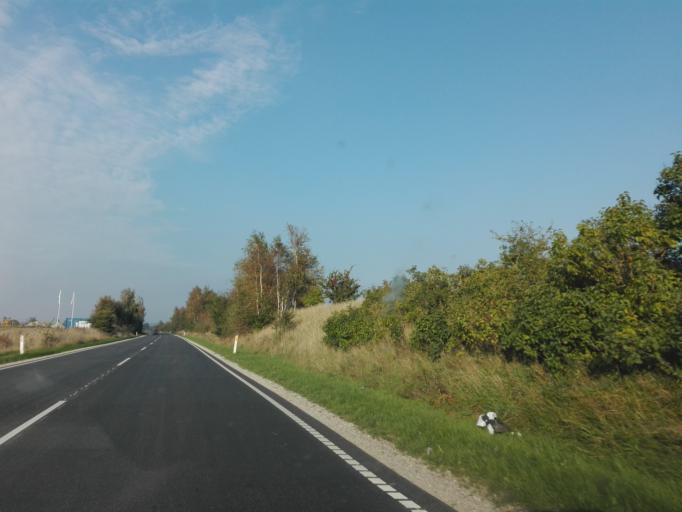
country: DK
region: Central Jutland
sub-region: Arhus Kommune
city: Malling
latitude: 56.0455
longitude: 10.1887
